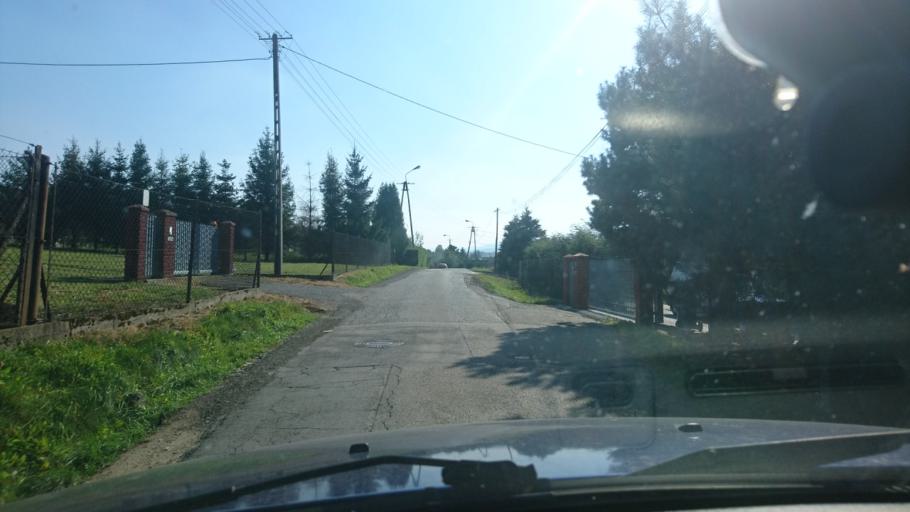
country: PL
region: Silesian Voivodeship
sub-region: Bielsko-Biala
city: Bielsko-Biala
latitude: 49.8460
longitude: 19.0758
